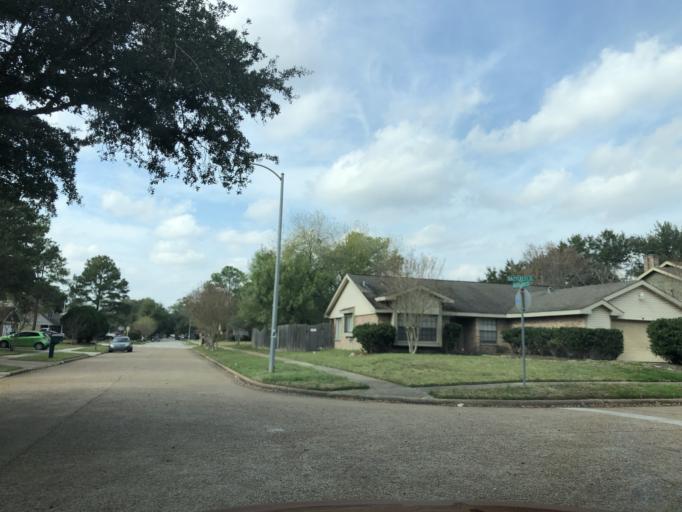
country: US
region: Texas
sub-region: Harris County
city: Tomball
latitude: 30.0354
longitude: -95.5413
